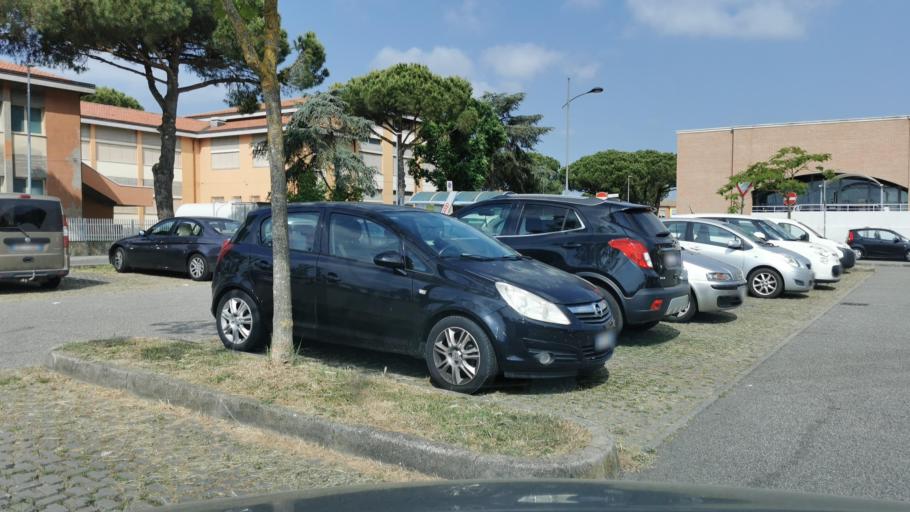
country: IT
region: Emilia-Romagna
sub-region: Provincia di Ferrara
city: Comacchio
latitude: 44.6915
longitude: 12.1841
